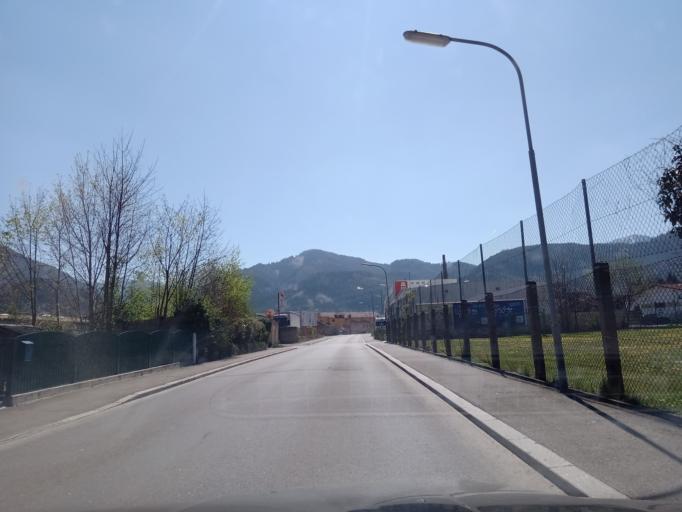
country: AT
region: Styria
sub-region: Politischer Bezirk Leoben
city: Leoben
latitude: 47.3700
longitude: 15.0874
